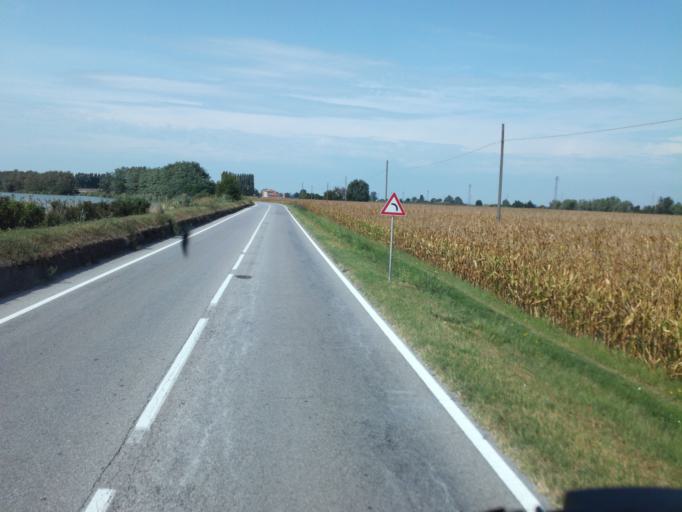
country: IT
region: Veneto
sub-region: Provincia di Rovigo
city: Bottrighe
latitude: 45.0521
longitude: 12.1189
